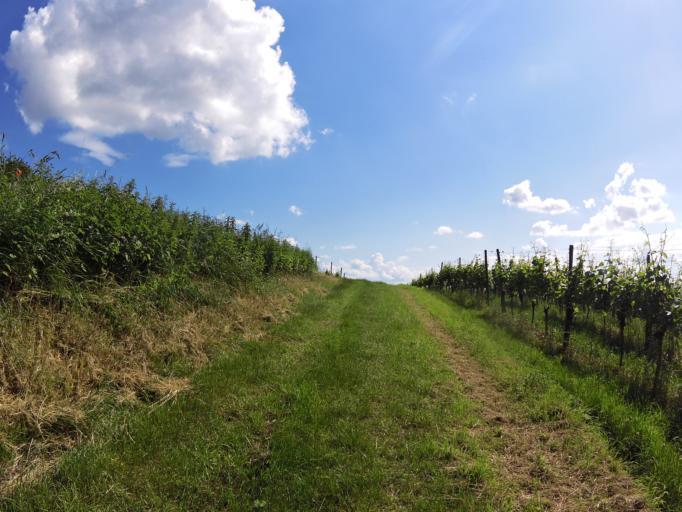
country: DE
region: Baden-Wuerttemberg
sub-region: Freiburg Region
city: Lahr
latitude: 48.3481
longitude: 7.8551
